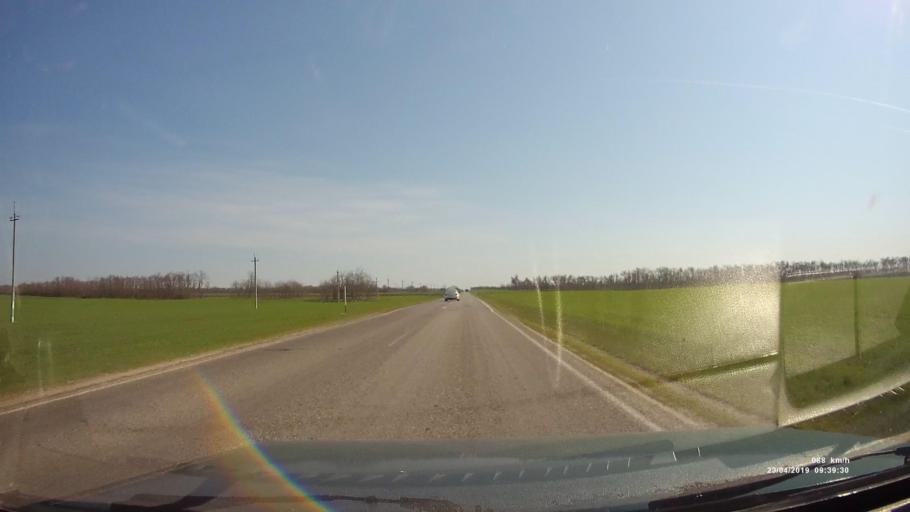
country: RU
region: Rostov
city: Gundorovskiy
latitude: 46.8540
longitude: 41.9272
